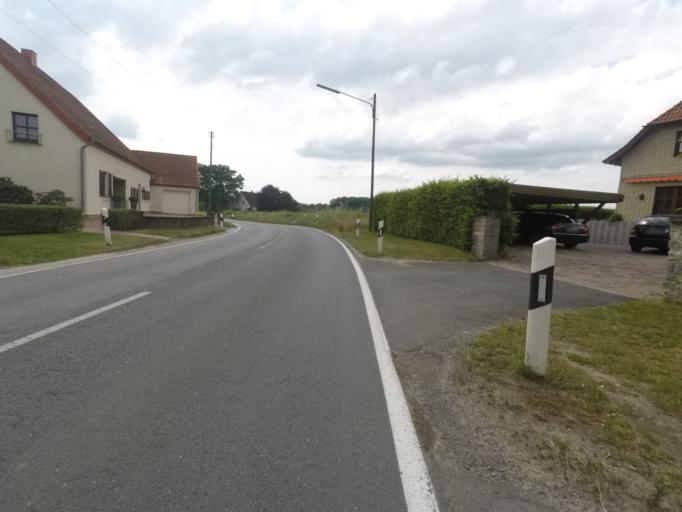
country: DE
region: North Rhine-Westphalia
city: Spenge
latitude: 52.1494
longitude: 8.4828
